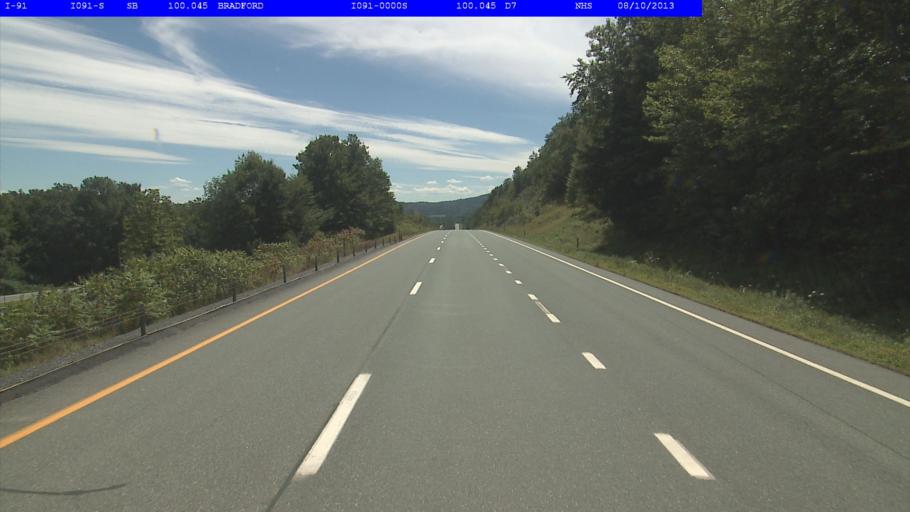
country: US
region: New Hampshire
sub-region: Grafton County
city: Haverhill
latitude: 44.0161
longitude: -72.1214
